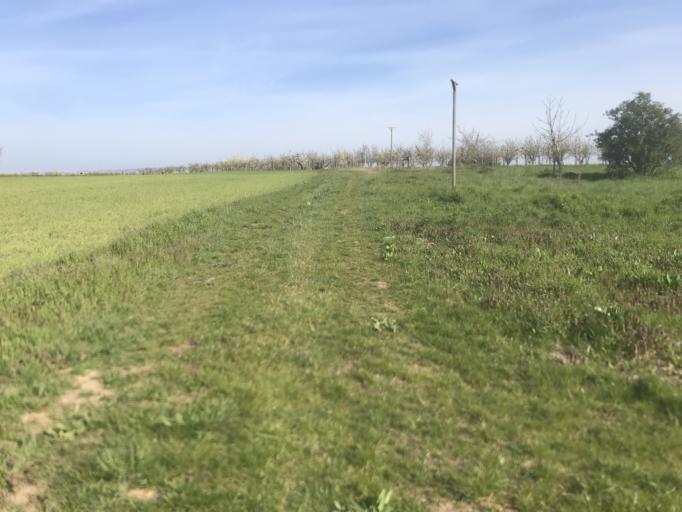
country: DE
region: Rheinland-Pfalz
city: Wackernheim
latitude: 49.9523
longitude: 8.1147
